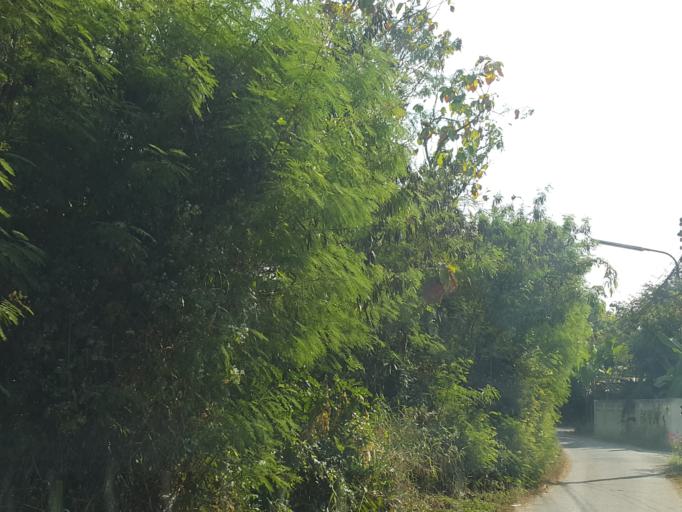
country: TH
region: Chiang Mai
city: San Sai
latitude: 18.8431
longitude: 99.0987
